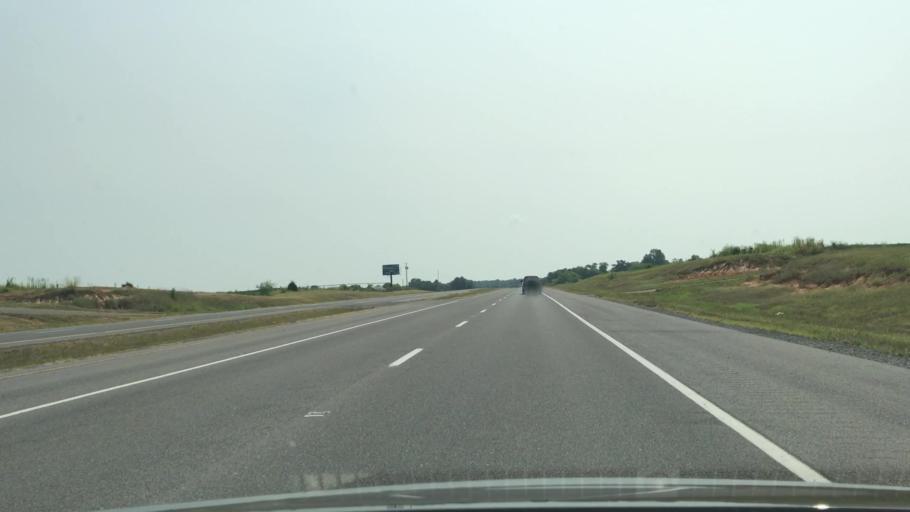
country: US
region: Kentucky
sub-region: Calloway County
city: Murray
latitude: 36.6498
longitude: -88.2587
